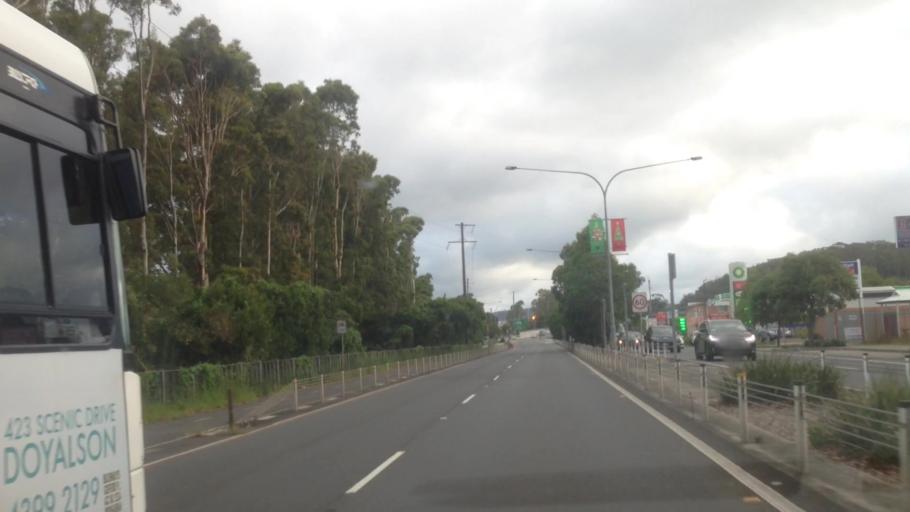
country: AU
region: New South Wales
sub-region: Wyong Shire
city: Chittaway Bay
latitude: -33.3046
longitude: 151.4205
